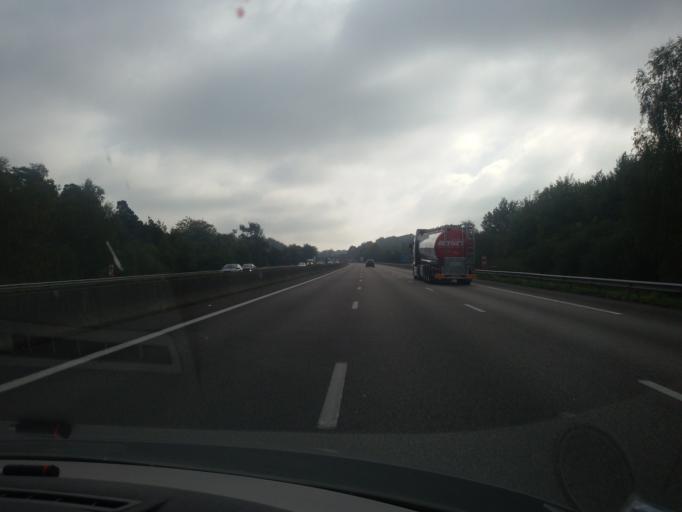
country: FR
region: Haute-Normandie
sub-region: Departement de l'Eure
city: Criquebeuf-sur-Seine
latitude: 49.2837
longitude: 1.1265
